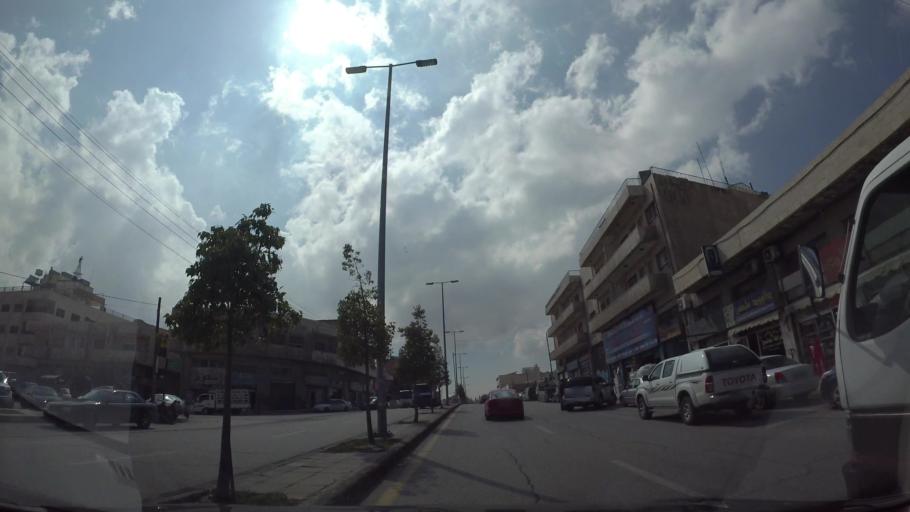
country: JO
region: Amman
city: Amman
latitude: 31.9847
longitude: 35.9959
